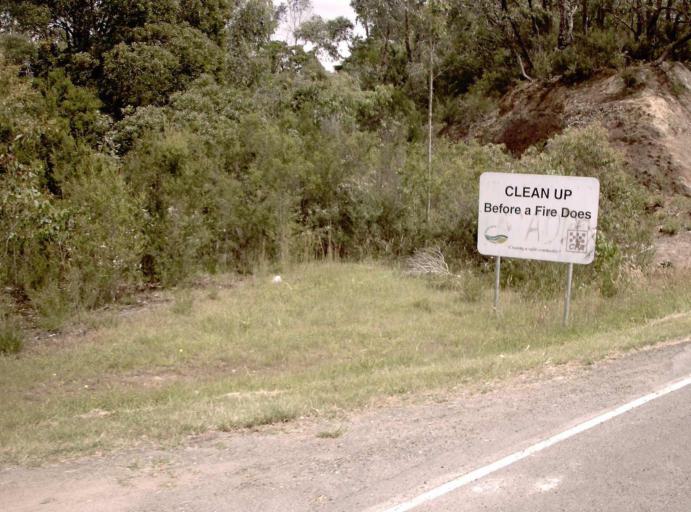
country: AU
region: Victoria
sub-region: Latrobe
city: Moe
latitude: -38.1051
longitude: 146.1581
